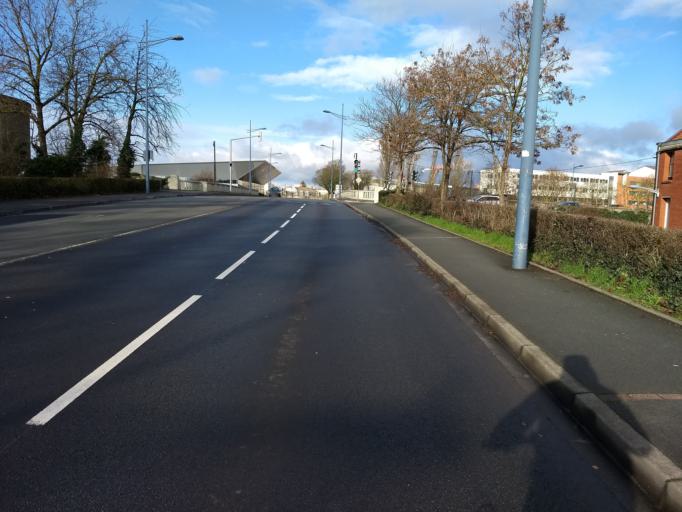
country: FR
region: Nord-Pas-de-Calais
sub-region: Departement du Pas-de-Calais
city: Arras
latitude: 50.2843
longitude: 2.7790
